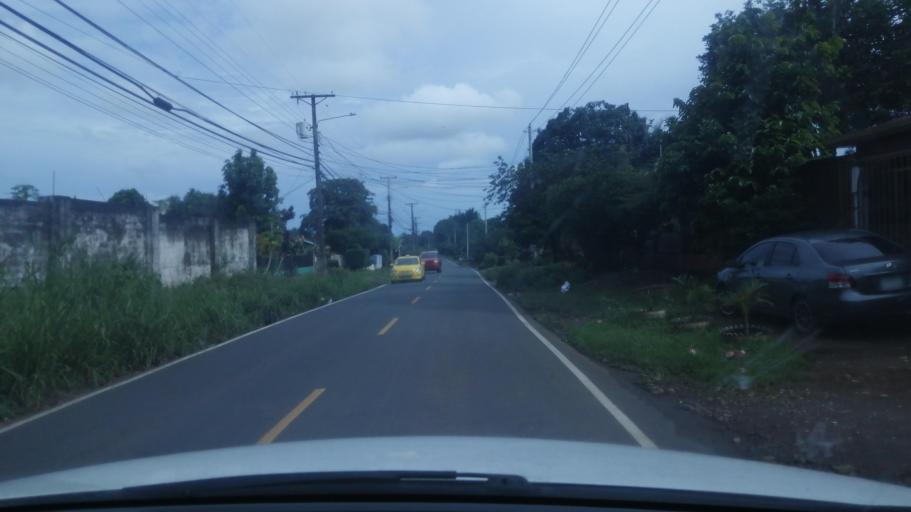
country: PA
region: Chiriqui
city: David
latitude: 8.4152
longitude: -82.4264
